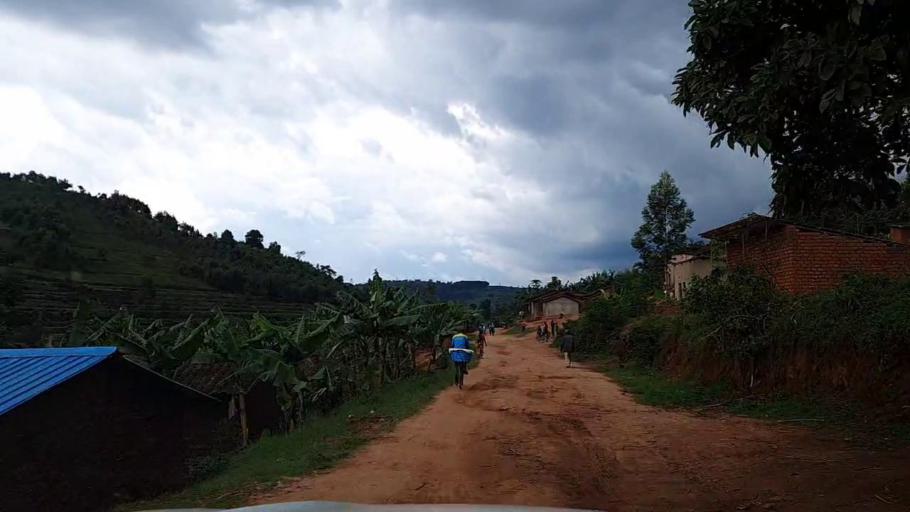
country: RW
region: Southern Province
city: Nyanza
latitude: -2.3923
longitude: 29.6874
